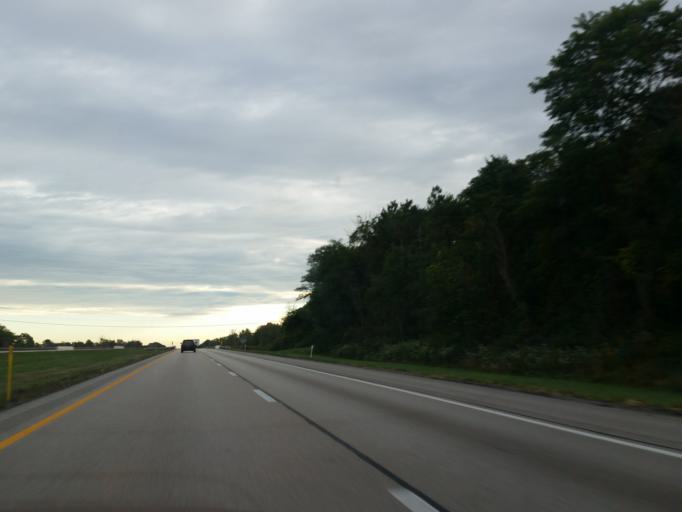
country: US
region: Ohio
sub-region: Ashtabula County
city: North Kingsville
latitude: 41.8982
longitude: -80.6255
